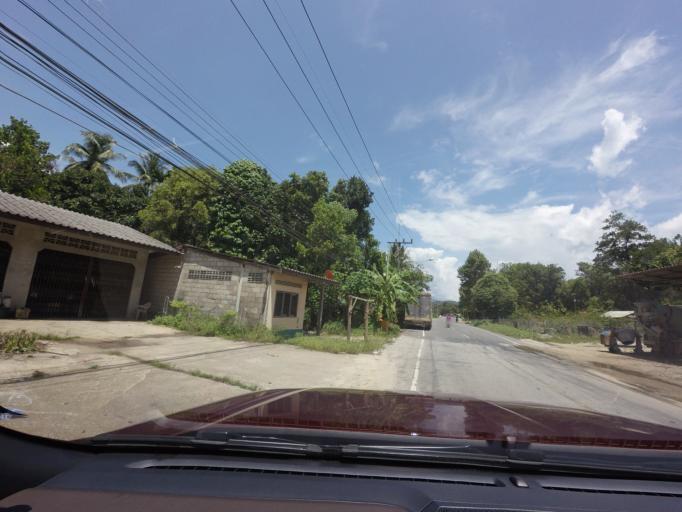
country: TH
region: Narathiwat
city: Chanae
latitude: 6.1252
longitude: 101.6978
